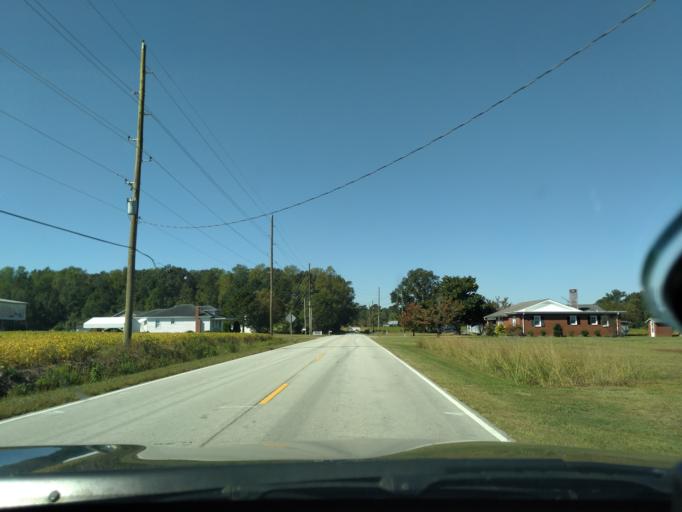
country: US
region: North Carolina
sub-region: Beaufort County
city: River Road
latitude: 35.5773
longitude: -76.9445
